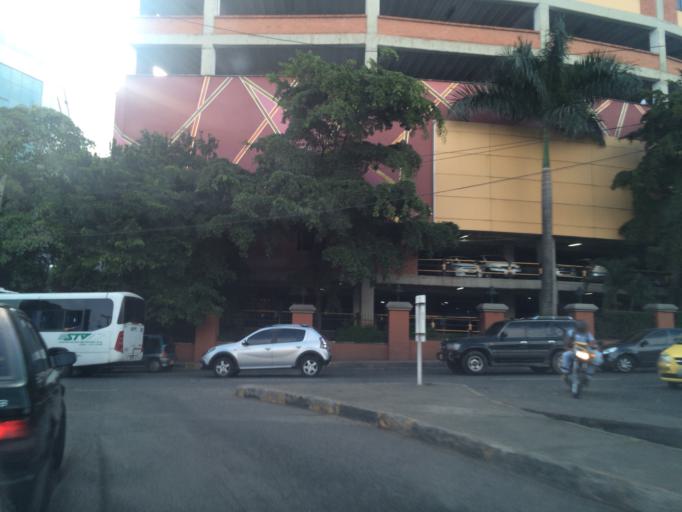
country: CO
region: Valle del Cauca
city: Cali
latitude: 3.4741
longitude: -76.5265
